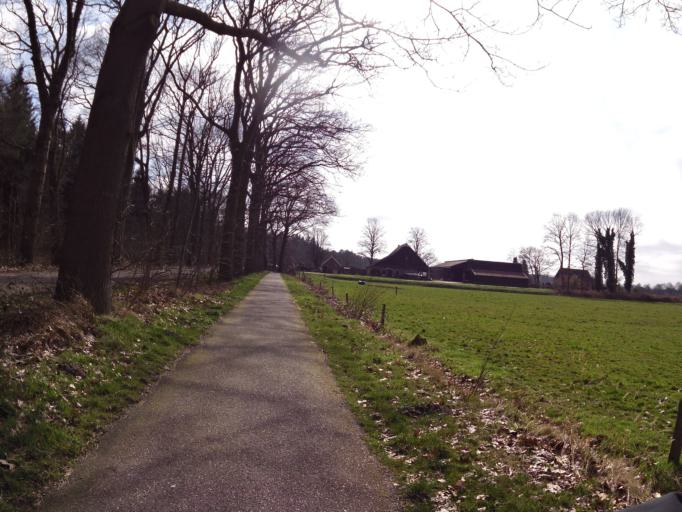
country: NL
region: Friesland
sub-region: Gemeente Weststellingwerf
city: Noordwolde
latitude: 52.8808
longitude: 6.2145
